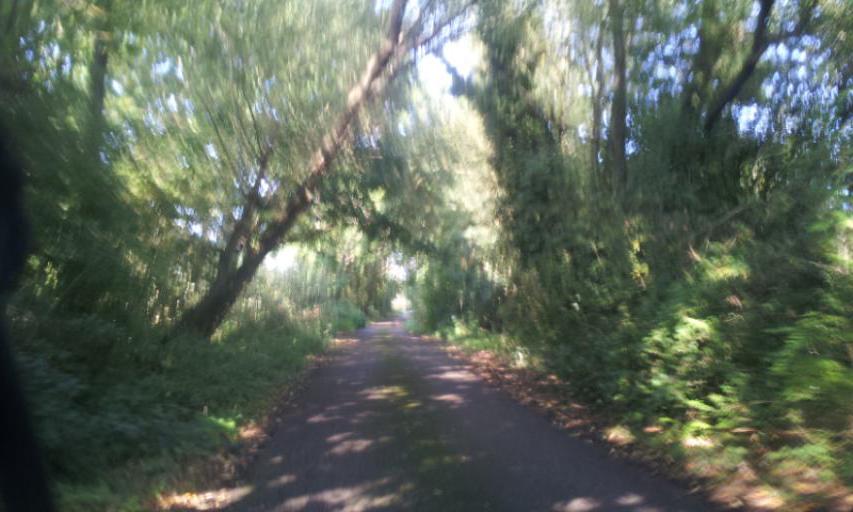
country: GB
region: England
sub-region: Kent
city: Hadlow
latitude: 51.2322
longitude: 0.3348
